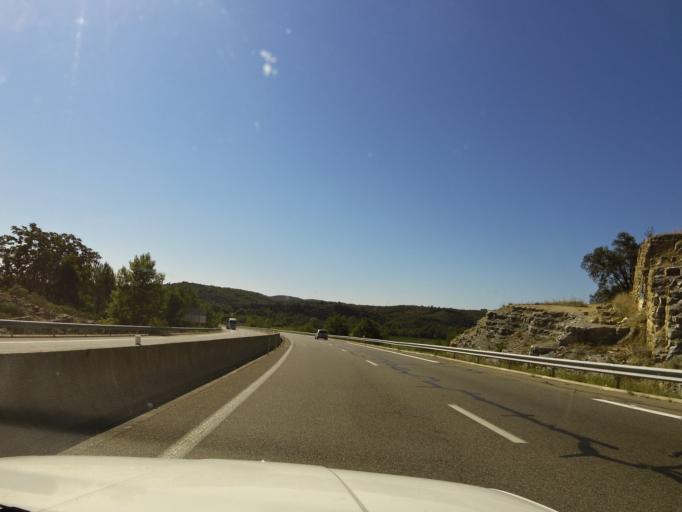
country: FR
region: Languedoc-Roussillon
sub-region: Departement du Gard
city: Vezenobres
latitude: 44.0220
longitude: 4.1472
